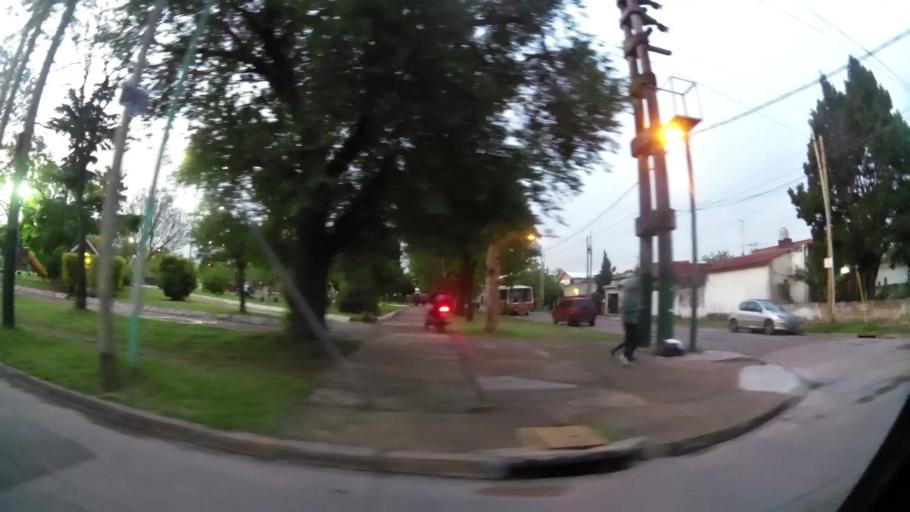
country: AR
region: Buenos Aires
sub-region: Partido de Lomas de Zamora
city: Lomas de Zamora
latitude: -34.7465
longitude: -58.3687
